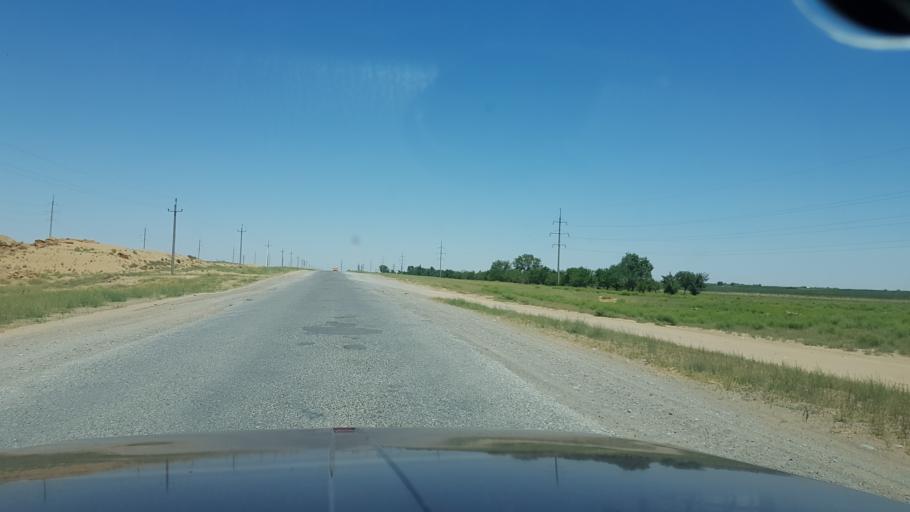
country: TM
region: Ahal
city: Annau
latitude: 37.8736
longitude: 58.7213
